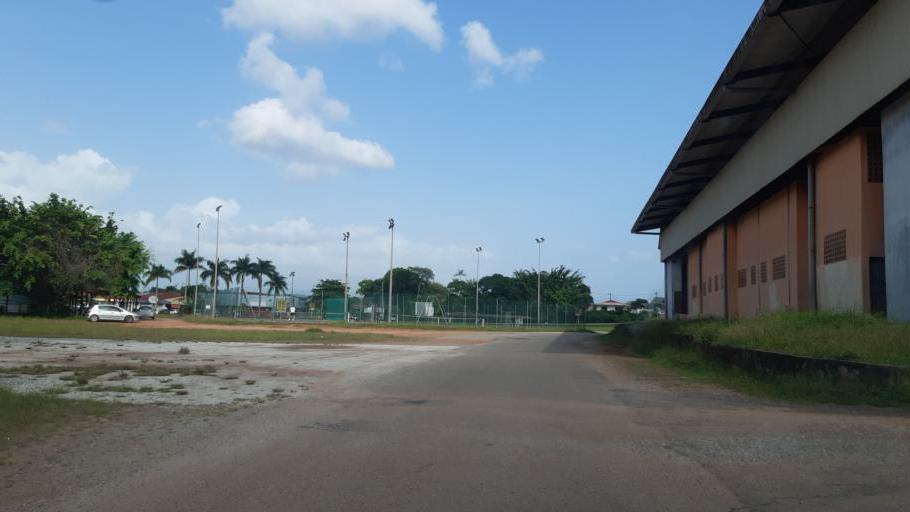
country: GF
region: Guyane
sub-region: Guyane
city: Matoury
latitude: 4.8476
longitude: -52.3277
